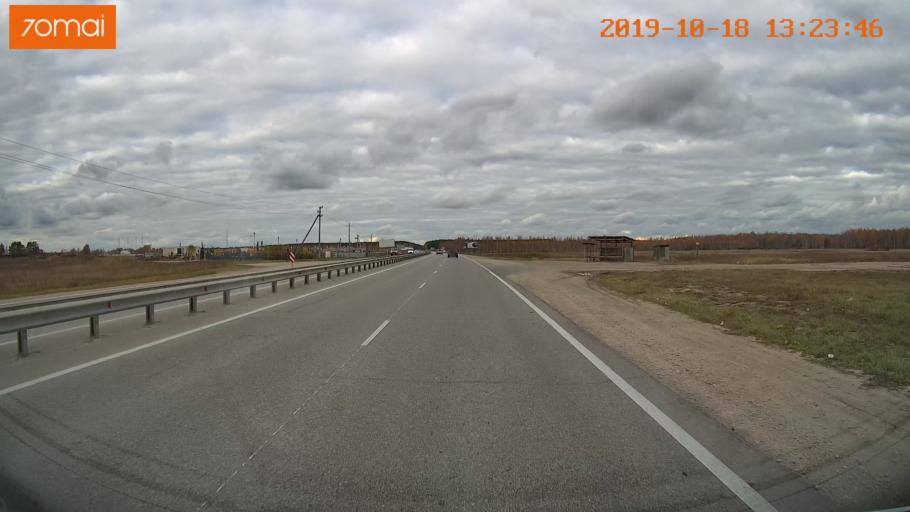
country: RU
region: Rjazan
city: Polyany
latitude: 54.7211
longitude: 39.8476
